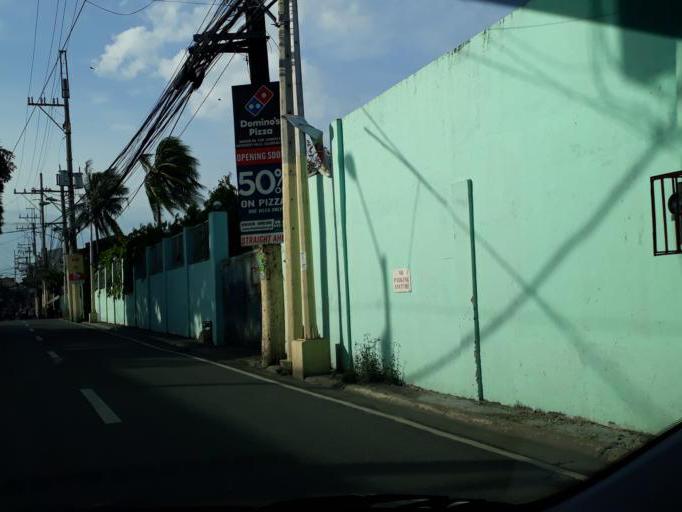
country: PH
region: Metro Manila
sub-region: Caloocan City
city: Niugan
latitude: 14.6457
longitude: 120.9743
